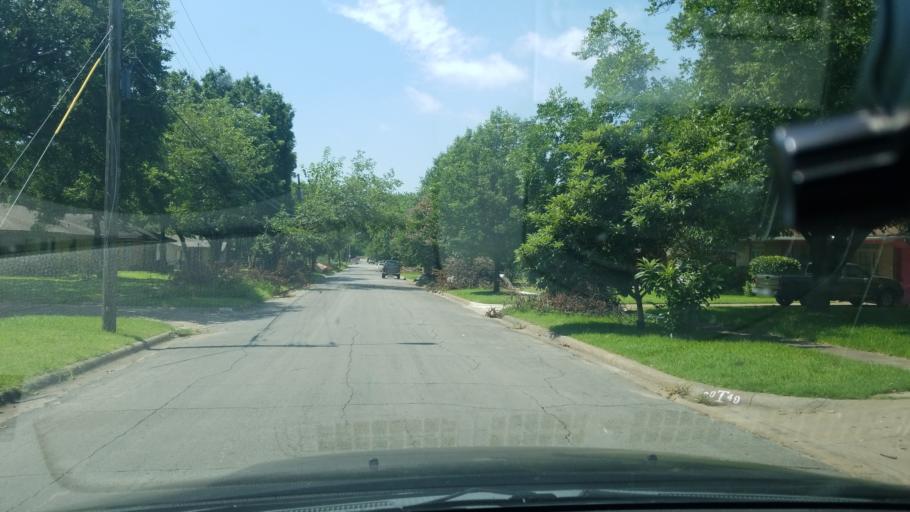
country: US
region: Texas
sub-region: Dallas County
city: Balch Springs
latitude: 32.7481
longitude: -96.6845
